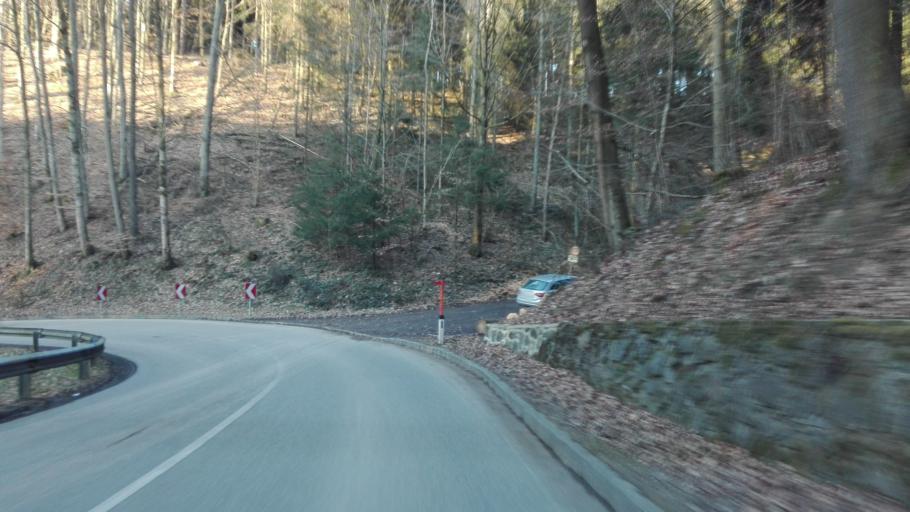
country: AT
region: Upper Austria
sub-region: Politischer Bezirk Linz-Land
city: Leonding
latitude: 48.3038
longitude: 14.2366
